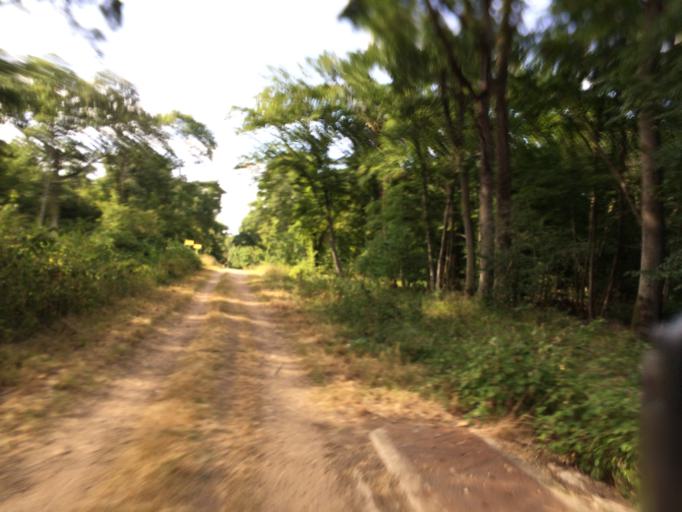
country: FR
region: Ile-de-France
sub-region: Departement de l'Essonne
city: Etiolles
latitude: 48.6429
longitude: 2.4901
